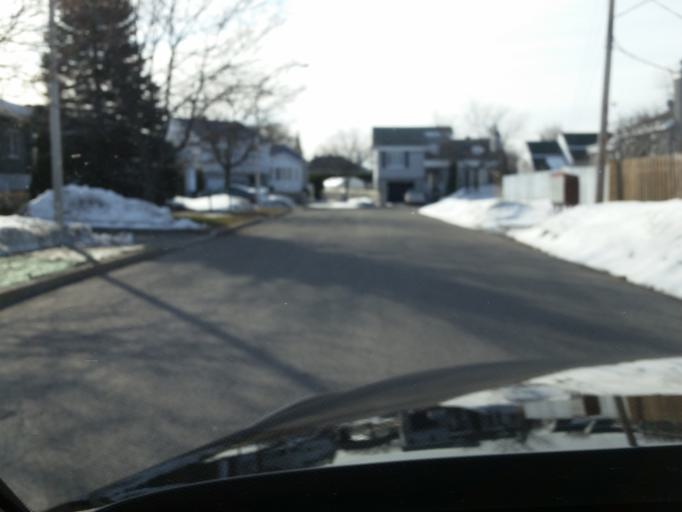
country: CA
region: Quebec
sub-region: Laurentides
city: Blainville
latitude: 45.6863
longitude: -73.9032
